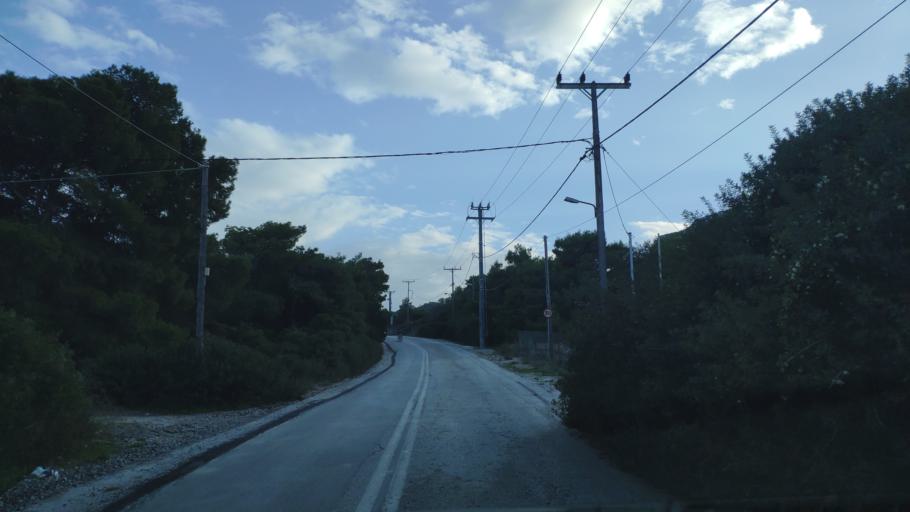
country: GR
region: Attica
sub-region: Nomarchia Anatolikis Attikis
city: Limin Mesoyaias
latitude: 37.9180
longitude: 24.0127
